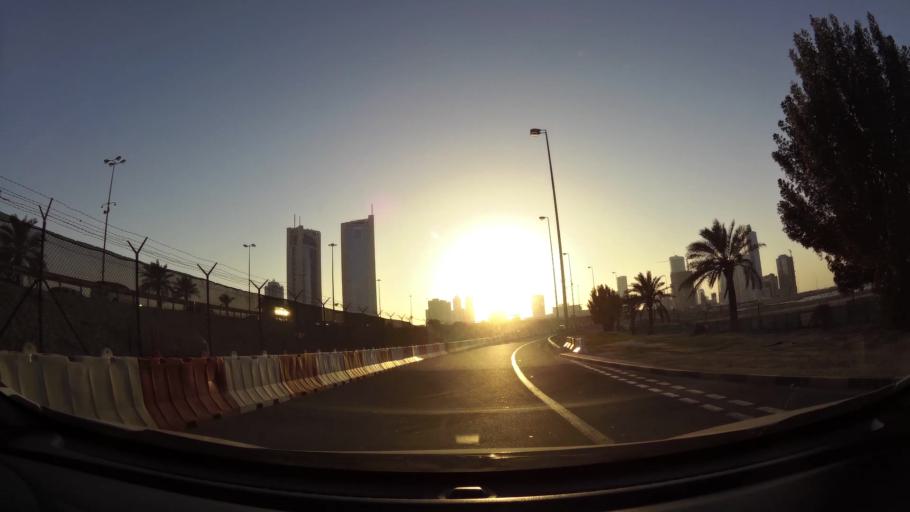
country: BH
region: Manama
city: Jidd Hafs
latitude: 26.2331
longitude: 50.5644
